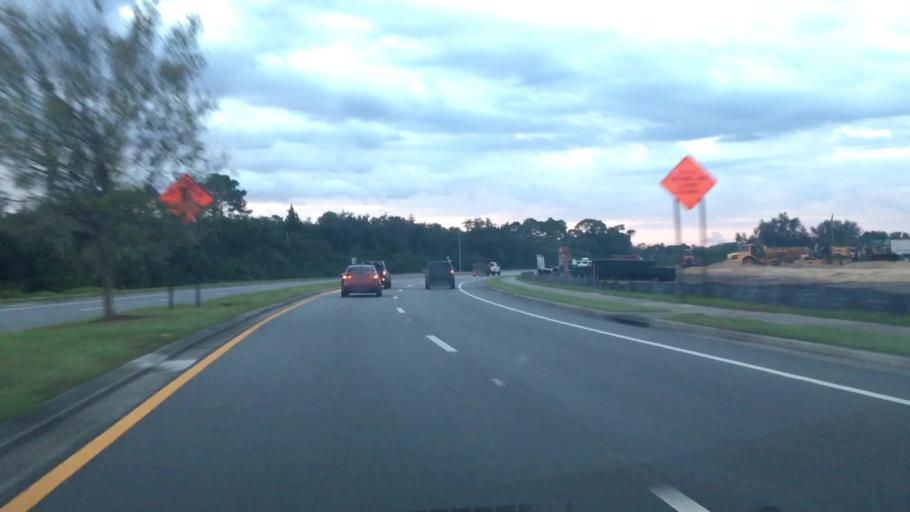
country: US
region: Florida
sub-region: Seminole County
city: Midway
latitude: 28.7822
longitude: -81.2111
